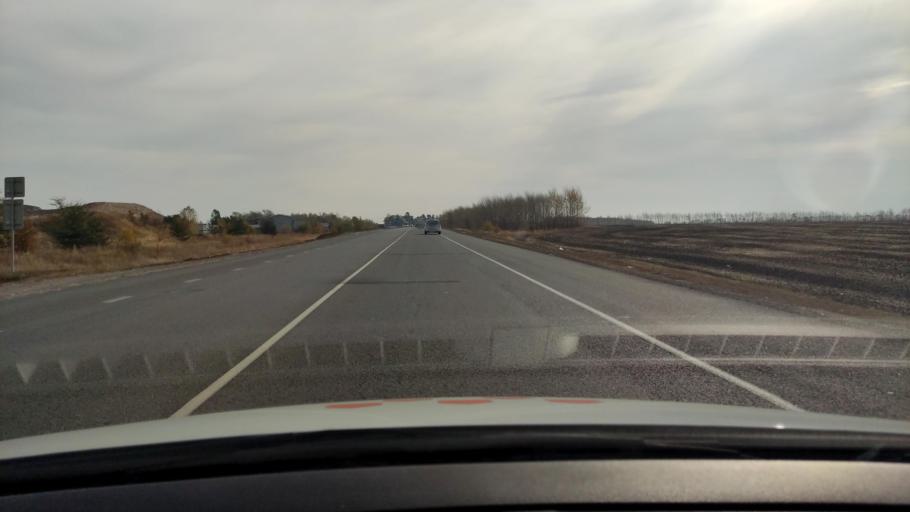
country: RU
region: Voronezj
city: Novaya Usman'
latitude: 51.6869
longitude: 39.4725
